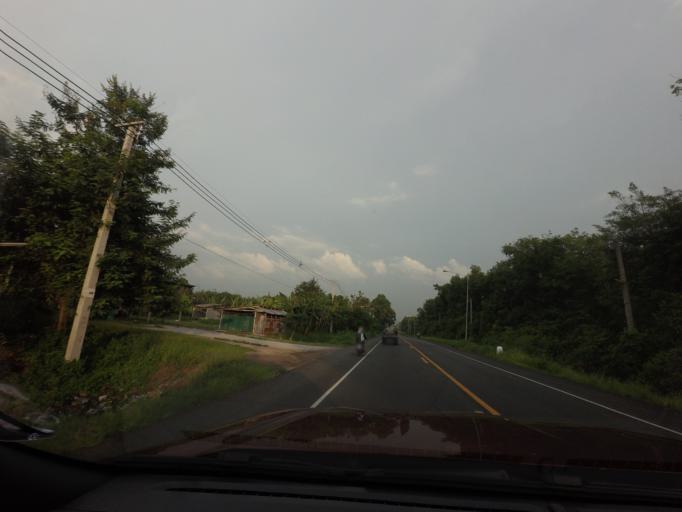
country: TH
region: Pattani
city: Mae Lan
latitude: 6.6570
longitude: 101.1717
